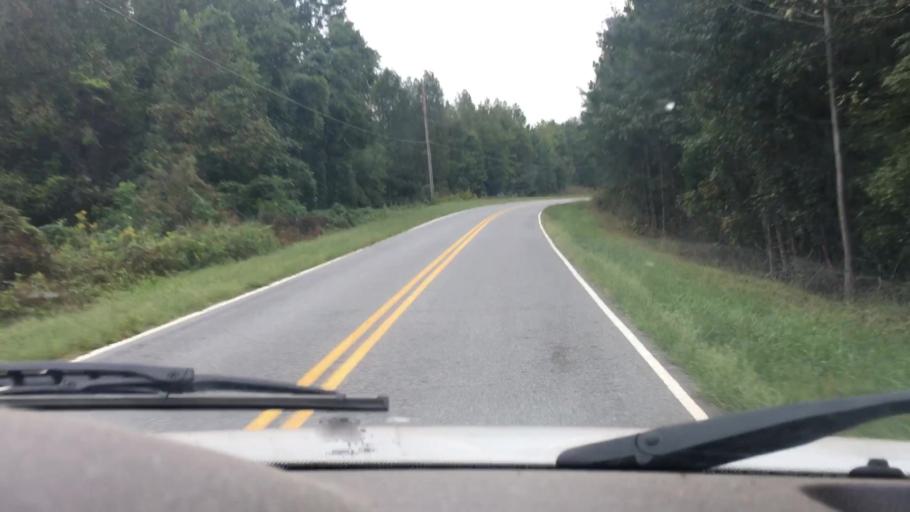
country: US
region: North Carolina
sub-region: Lincoln County
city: Denver
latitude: 35.5066
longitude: -81.0214
